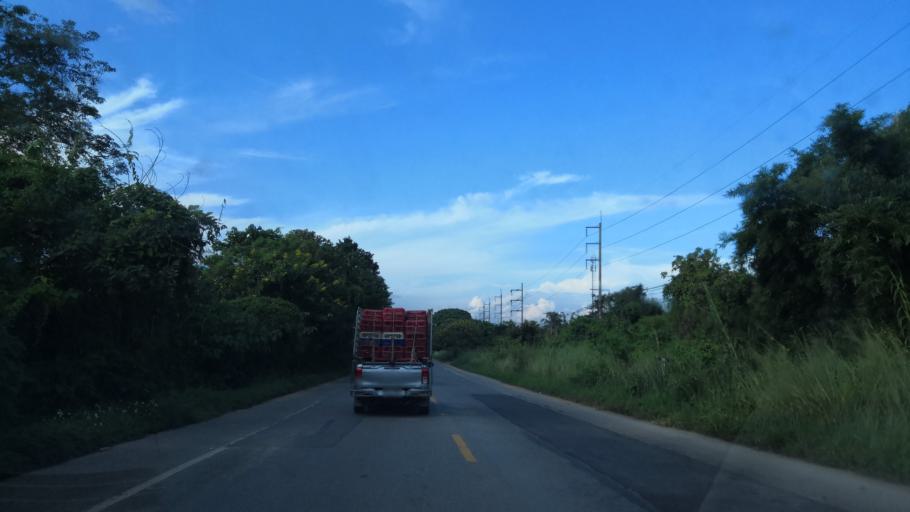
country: TH
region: Chiang Rai
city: Mae Suai
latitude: 19.5174
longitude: 99.4787
